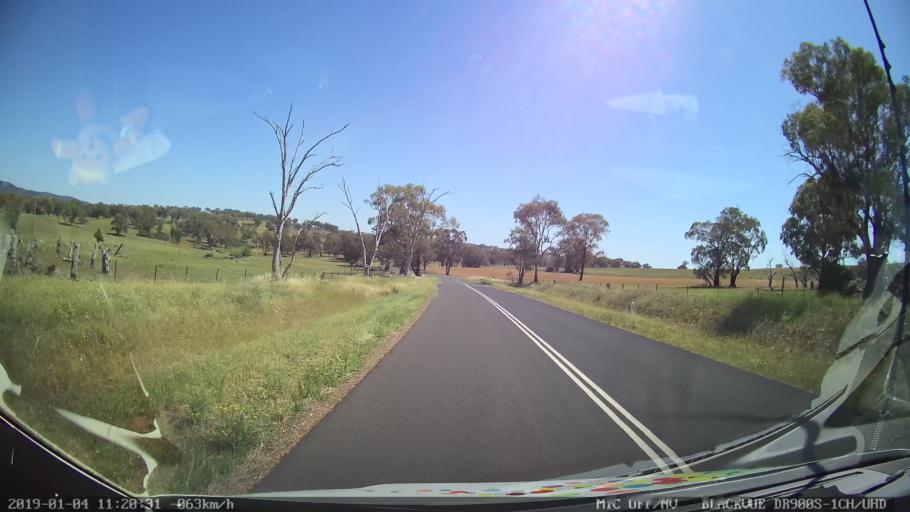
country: AU
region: New South Wales
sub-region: Cabonne
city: Molong
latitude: -33.1630
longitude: 148.7066
